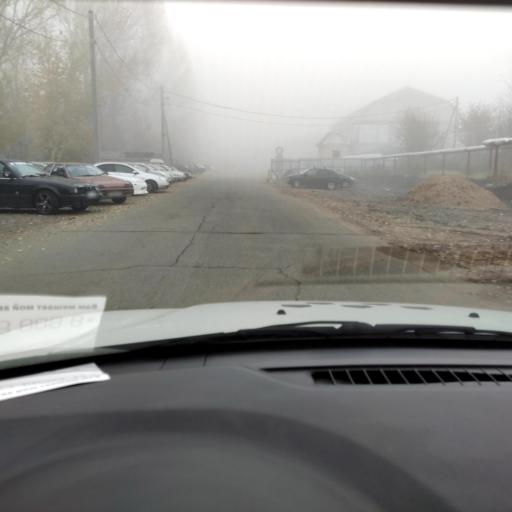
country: RU
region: Samara
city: Tol'yatti
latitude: 53.5444
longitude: 49.2921
